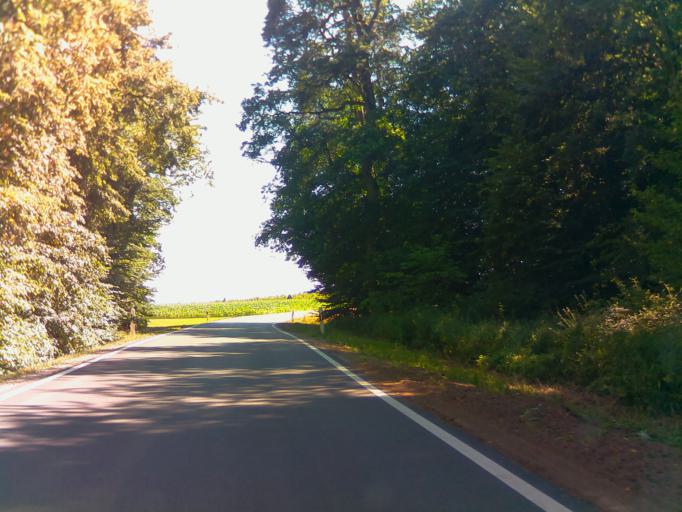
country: DE
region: Bavaria
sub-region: Regierungsbezirk Unterfranken
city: Neunkirchen
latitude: 49.7236
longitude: 9.3714
